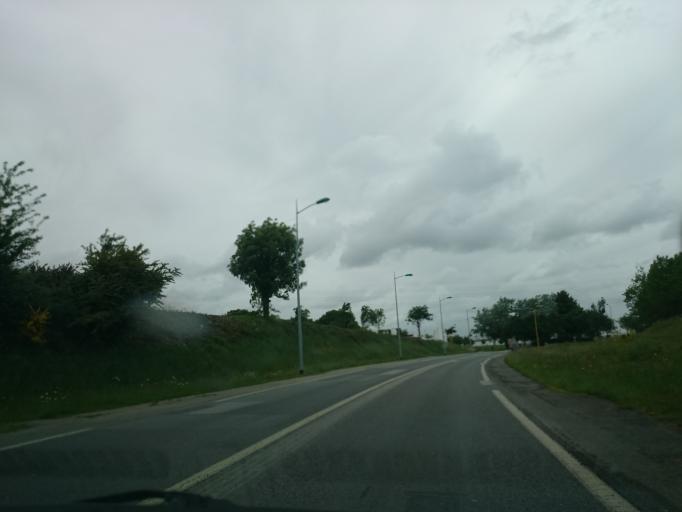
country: FR
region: Brittany
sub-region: Departement du Morbihan
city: Vannes
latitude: 47.6751
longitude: -2.7746
